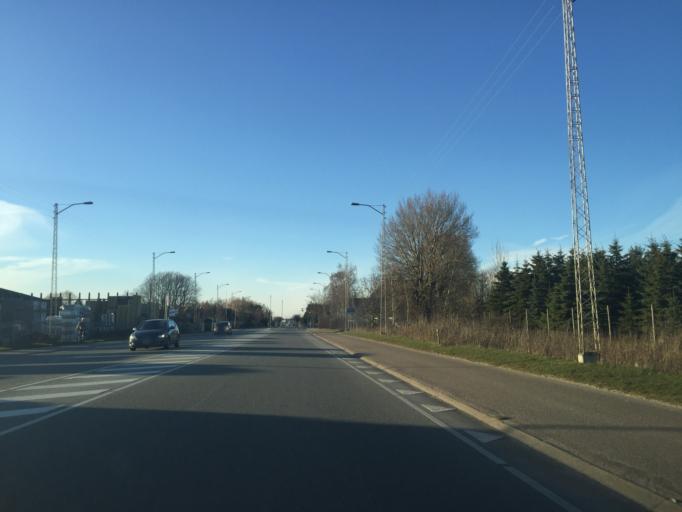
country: DK
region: Capital Region
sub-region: Tarnby Kommune
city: Tarnby
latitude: 55.6077
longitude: 12.6162
